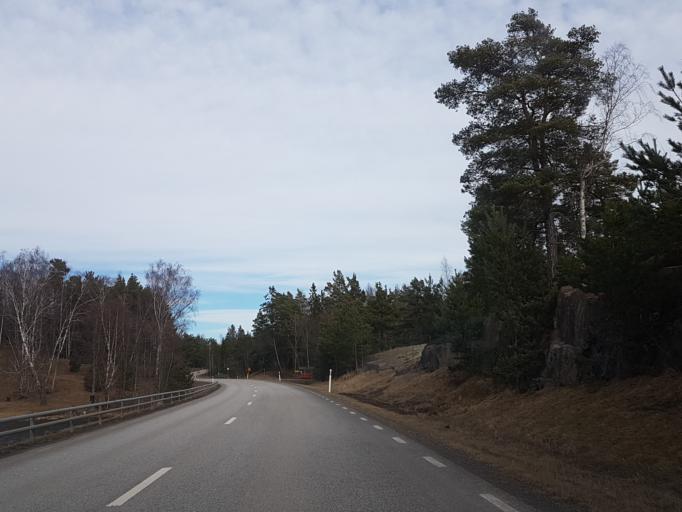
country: SE
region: Stockholm
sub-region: Norrtalje Kommun
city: Norrtalje
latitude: 59.6801
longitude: 18.8121
